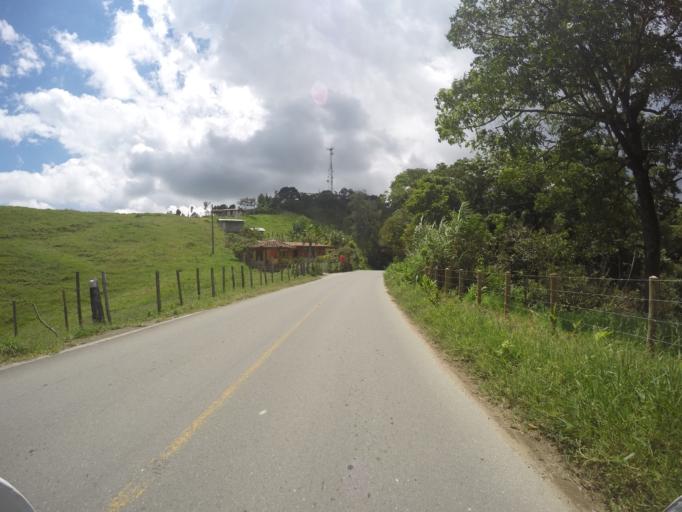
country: CO
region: Quindio
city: Filandia
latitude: 4.6551
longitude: -75.6759
